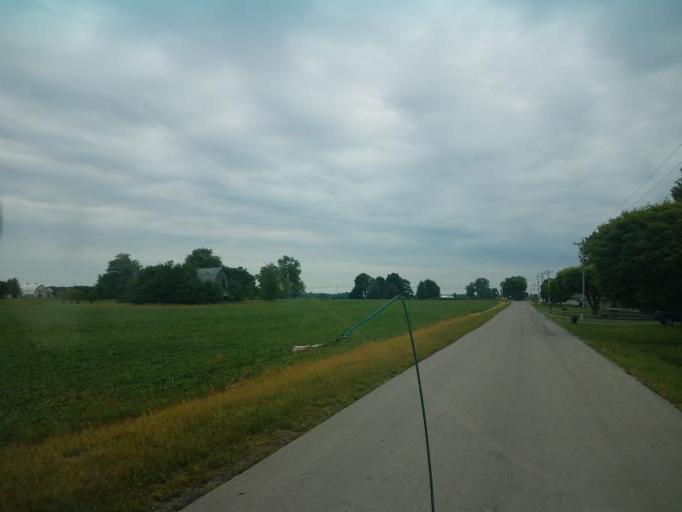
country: US
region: Ohio
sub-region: Hardin County
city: Ada
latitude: 40.7912
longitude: -83.8259
